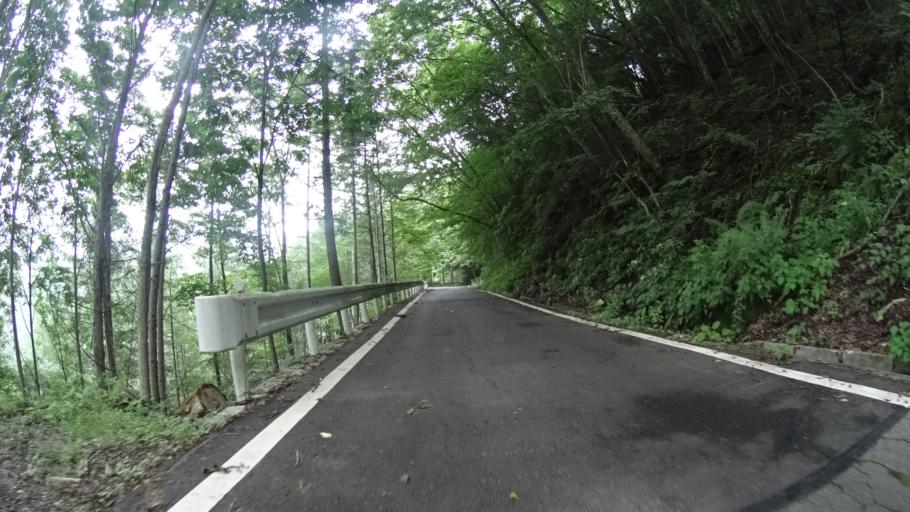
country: JP
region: Yamanashi
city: Kofu-shi
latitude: 35.8084
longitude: 138.6192
